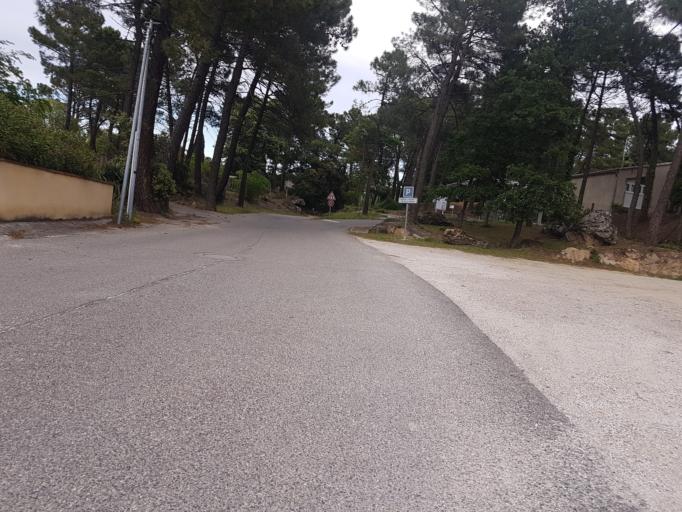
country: FR
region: Provence-Alpes-Cote d'Azur
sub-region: Departement du Vaucluse
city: Mondragon
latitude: 44.2436
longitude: 4.7284
